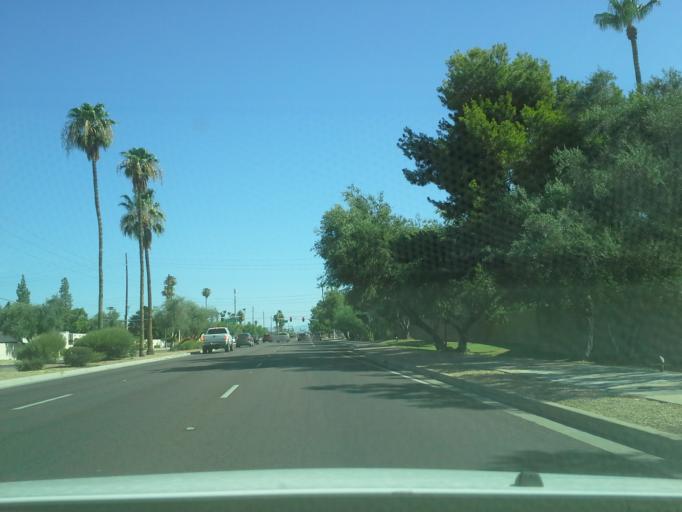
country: US
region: Arizona
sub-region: Maricopa County
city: Paradise Valley
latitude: 33.5225
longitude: -111.9258
